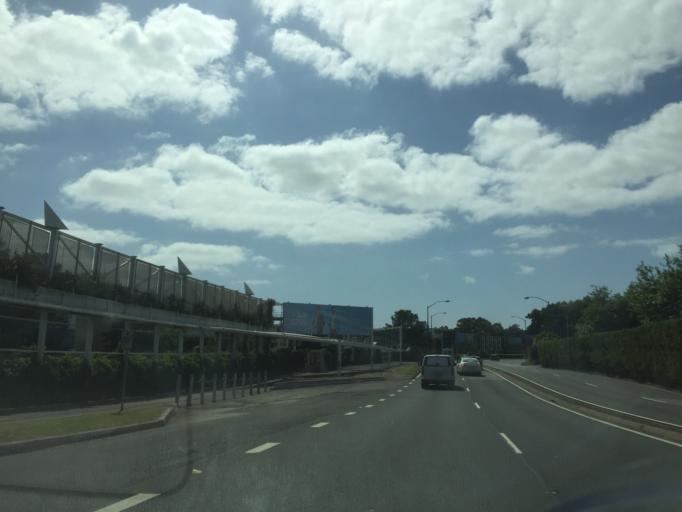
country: AU
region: New South Wales
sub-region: Botany Bay
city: Mascot
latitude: -33.9261
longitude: 151.1773
